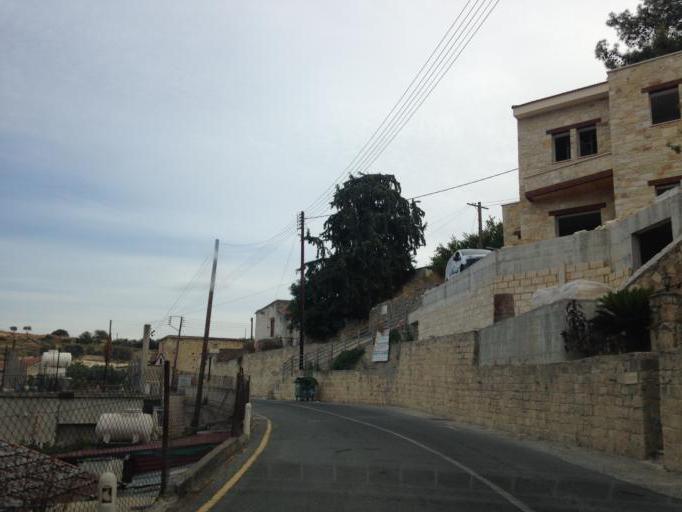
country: CY
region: Limassol
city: Pachna
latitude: 34.7801
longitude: 32.7966
